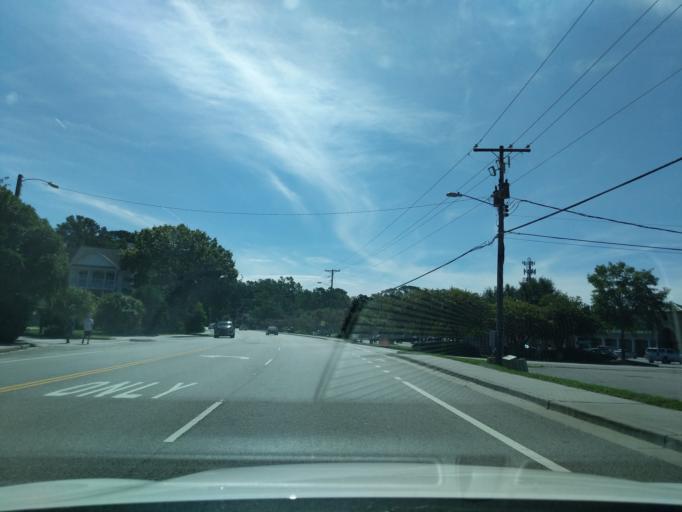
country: US
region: South Carolina
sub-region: Charleston County
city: Charleston
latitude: 32.7428
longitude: -79.9371
